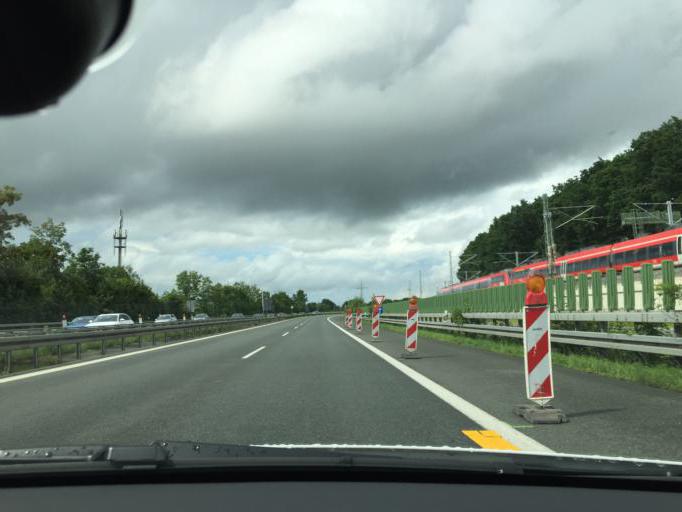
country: DE
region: Bavaria
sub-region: Regierungsbezirk Mittelfranken
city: Mohrendorf
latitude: 49.6169
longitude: 11.0016
